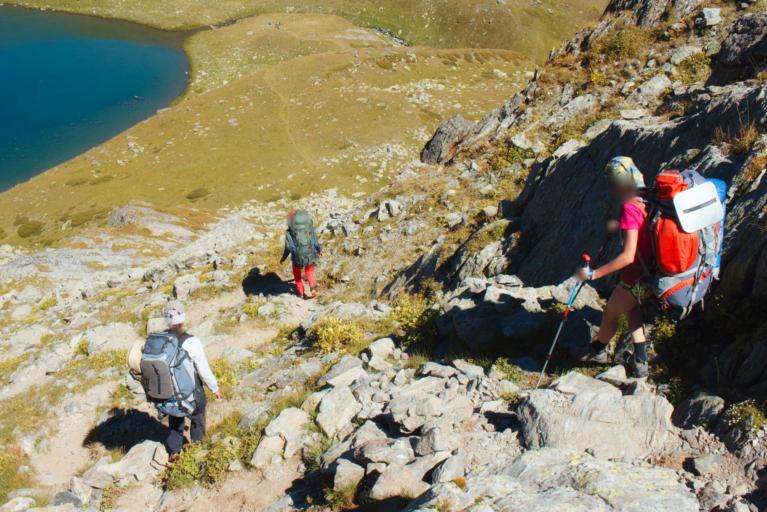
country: RU
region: Karachayevo-Cherkesiya
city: Mednogorskiy
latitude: 43.6206
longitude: 41.1127
